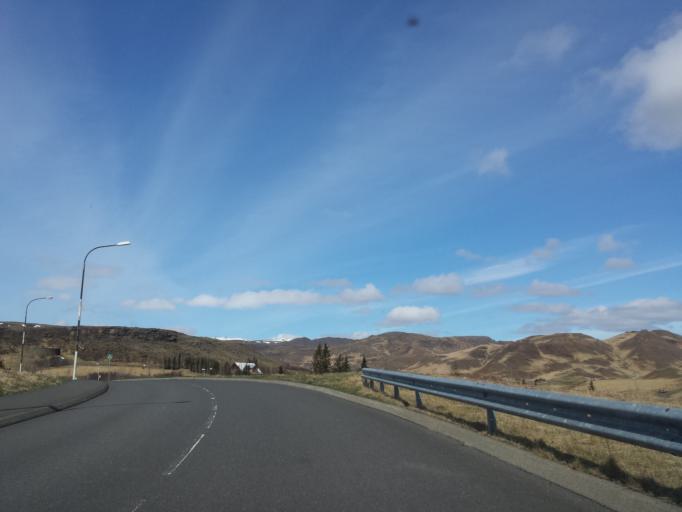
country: IS
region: South
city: Hveragerdi
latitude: 64.0053
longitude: -21.1852
